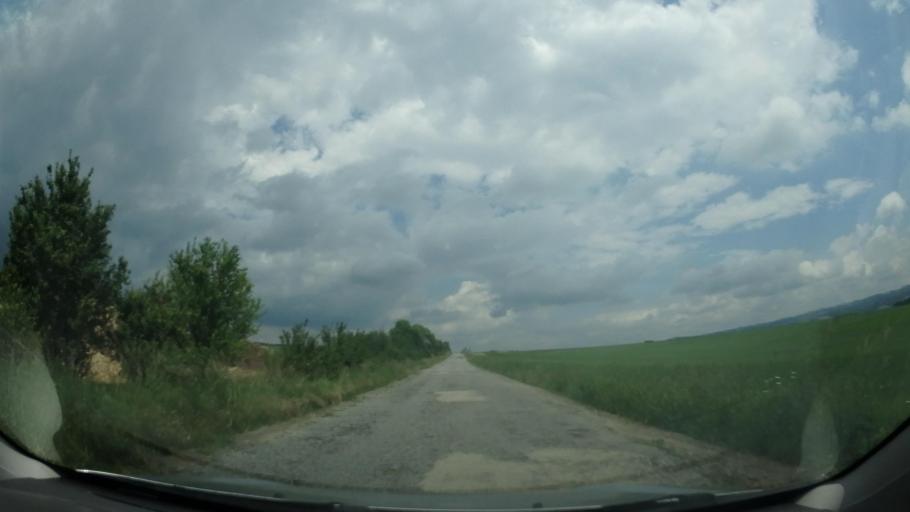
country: CZ
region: South Moravian
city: Boritov
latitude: 49.4357
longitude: 16.5951
